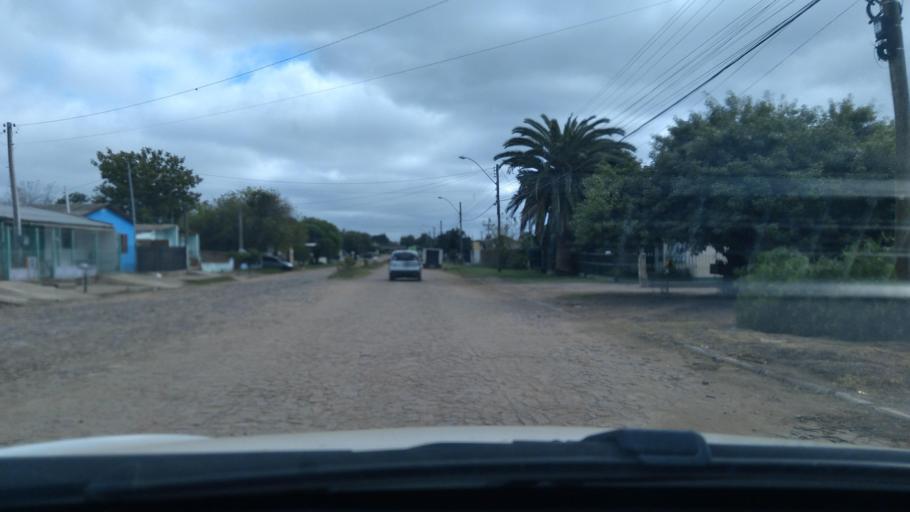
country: BR
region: Rio Grande do Sul
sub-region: Dom Pedrito
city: Dom Pedrito
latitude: -30.9809
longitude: -54.6593
